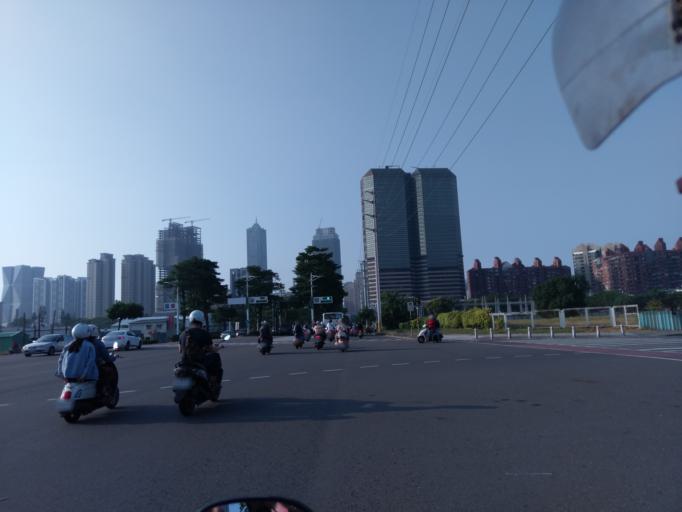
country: TW
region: Kaohsiung
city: Kaohsiung
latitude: 22.6018
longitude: 120.3117
